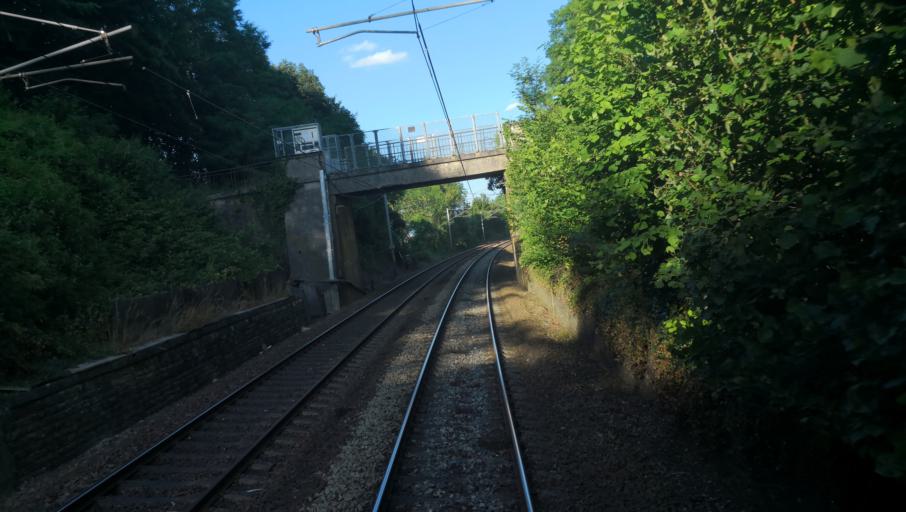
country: FR
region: Ile-de-France
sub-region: Departement des Yvelines
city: Rosny-sur-Seine
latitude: 48.9842
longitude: 1.6284
